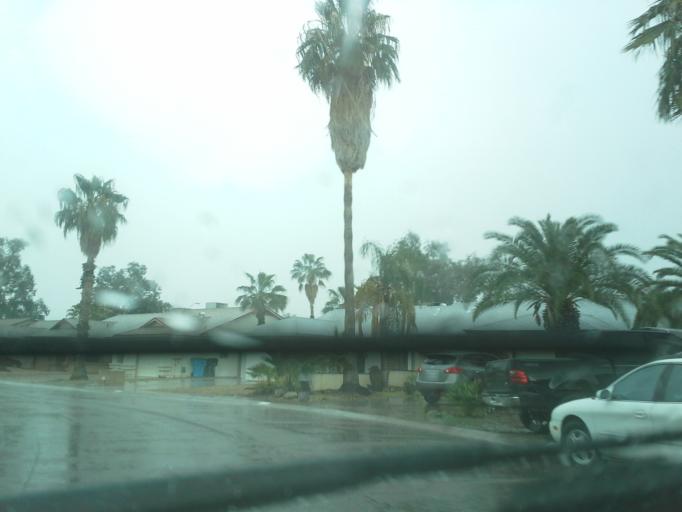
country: US
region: Arizona
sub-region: Maricopa County
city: Paradise Valley
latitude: 33.6336
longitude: -112.0442
